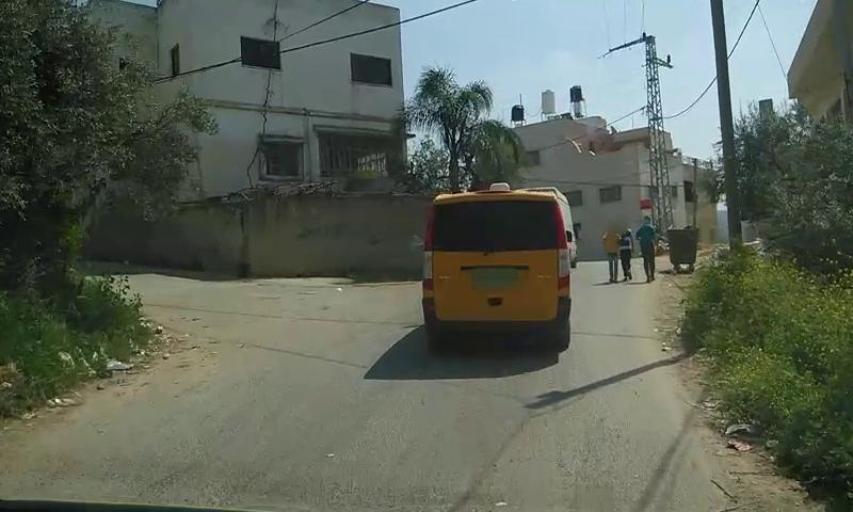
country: PS
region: West Bank
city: Bayta al Fawqa
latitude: 32.1436
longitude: 35.2777
